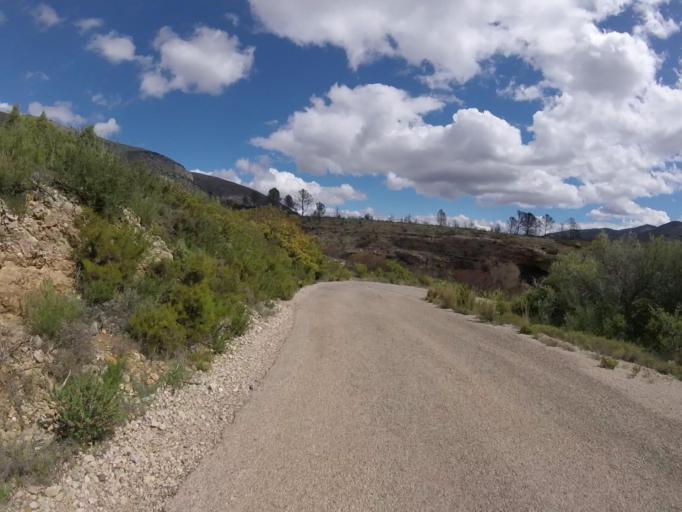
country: ES
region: Valencia
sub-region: Provincia de Castello
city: Sierra-Engarceran
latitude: 40.2867
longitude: -0.0672
